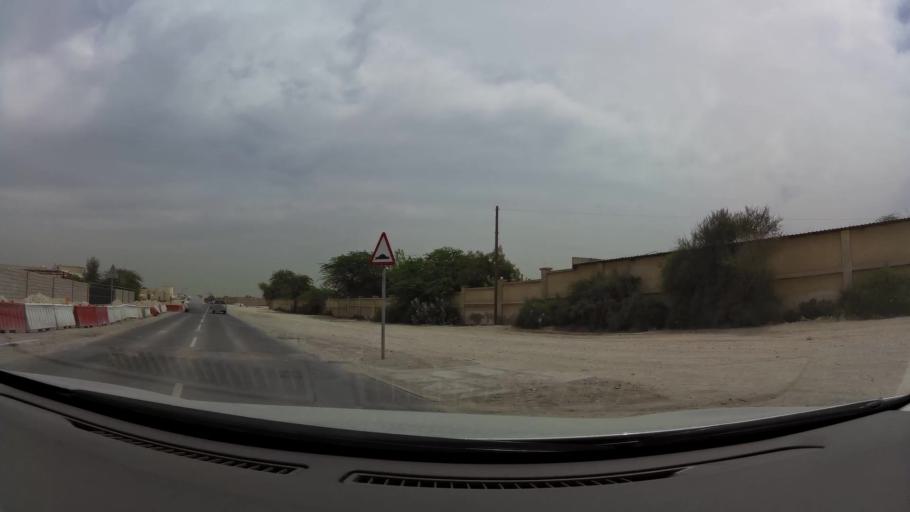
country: QA
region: Baladiyat ar Rayyan
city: Ar Rayyan
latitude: 25.2763
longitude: 51.4488
